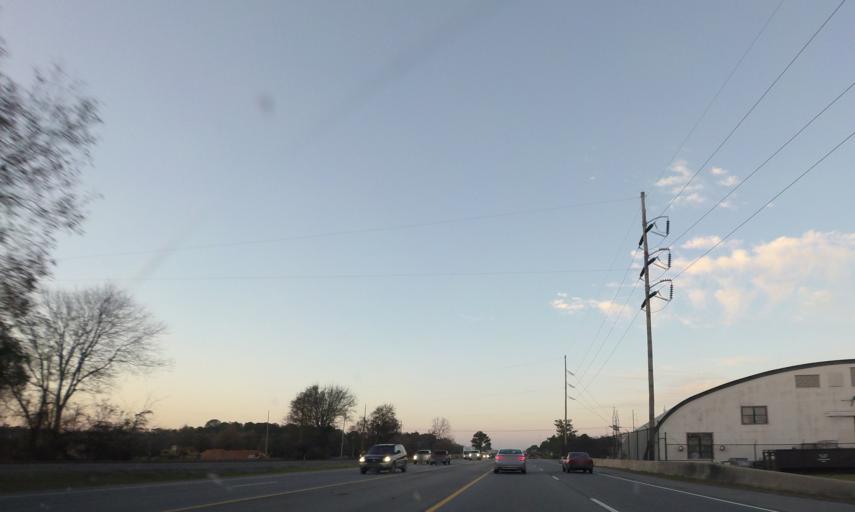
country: US
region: Georgia
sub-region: Houston County
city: Robins Air Force Base
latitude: 32.6041
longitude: -83.5942
